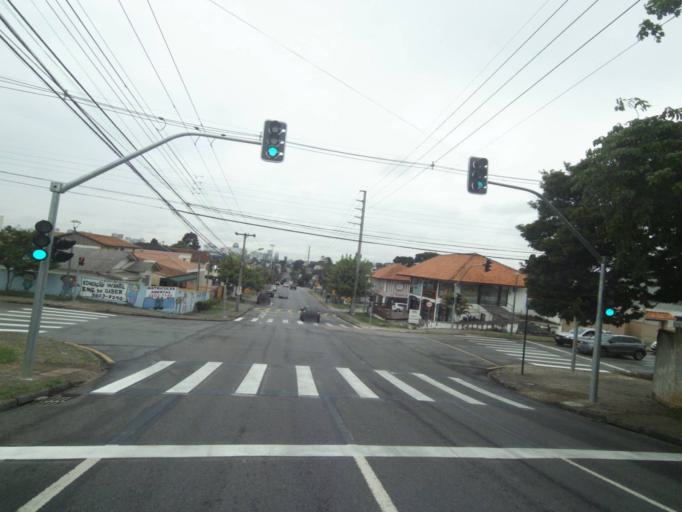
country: BR
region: Parana
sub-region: Curitiba
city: Curitiba
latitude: -25.4150
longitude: -49.2859
